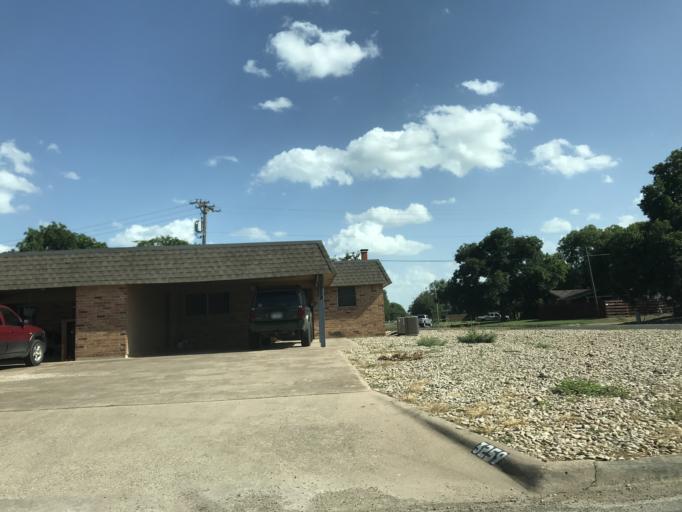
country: US
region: Texas
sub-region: Taylor County
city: Abilene
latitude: 32.4308
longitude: -99.7634
